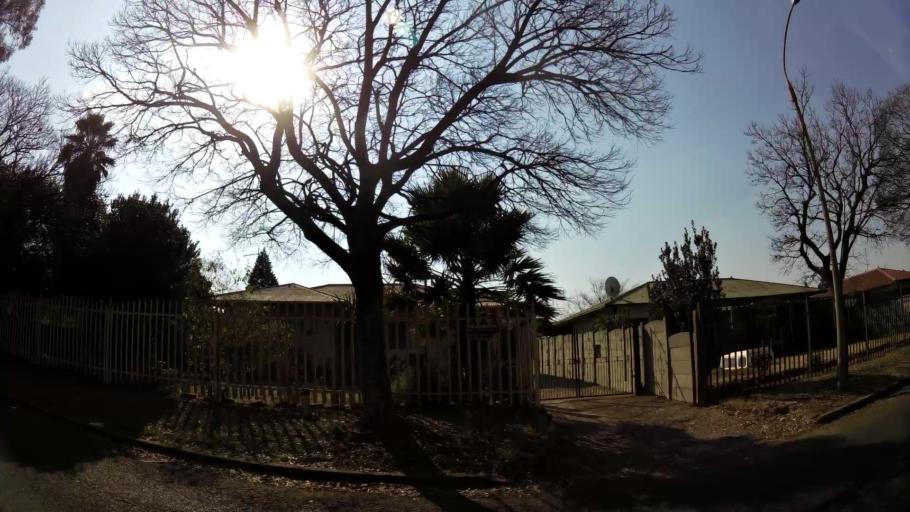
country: ZA
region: Gauteng
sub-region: Ekurhuleni Metropolitan Municipality
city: Boksburg
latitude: -26.2110
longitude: 28.2630
